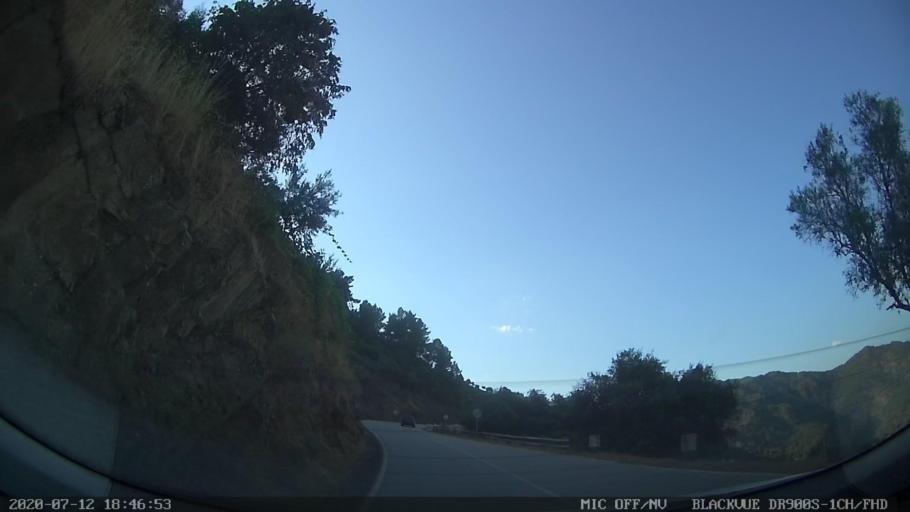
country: PT
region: Viseu
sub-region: Sao Joao da Pesqueira
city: Sao Joao da Pesqueira
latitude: 41.2324
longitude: -7.4291
